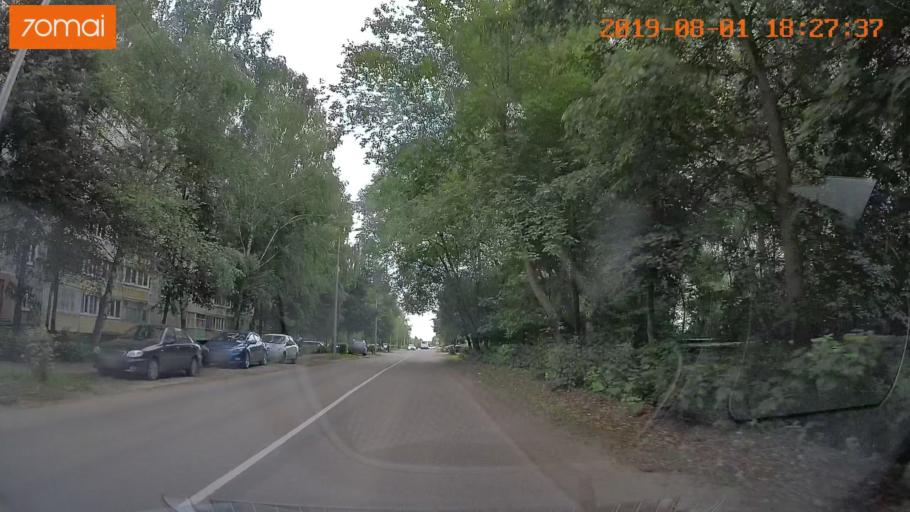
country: RU
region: Moskovskaya
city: Voskresensk
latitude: 55.3114
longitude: 38.6448
